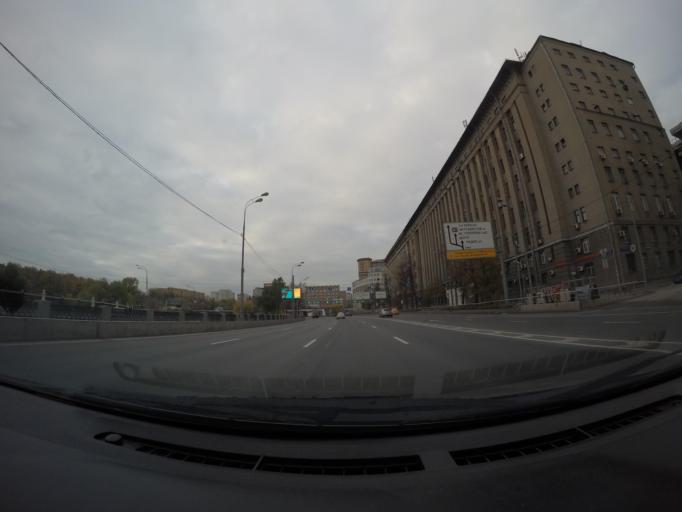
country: RU
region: Moscow
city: Lefortovo
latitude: 55.7722
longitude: 37.6770
